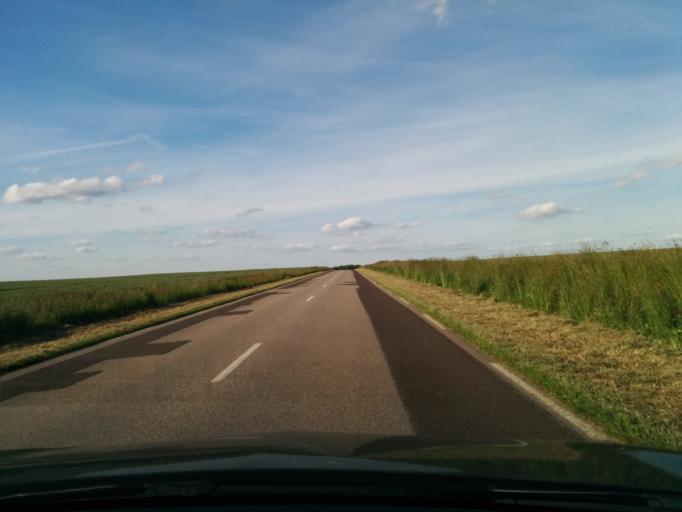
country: FR
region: Haute-Normandie
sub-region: Departement de l'Eure
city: Les Andelys
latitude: 49.2934
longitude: 1.4189
